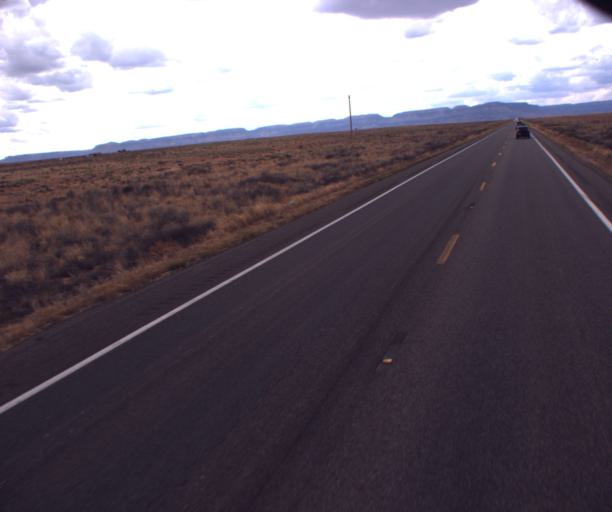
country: US
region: Arizona
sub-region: Navajo County
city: Kayenta
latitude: 36.7392
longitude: -110.0842
